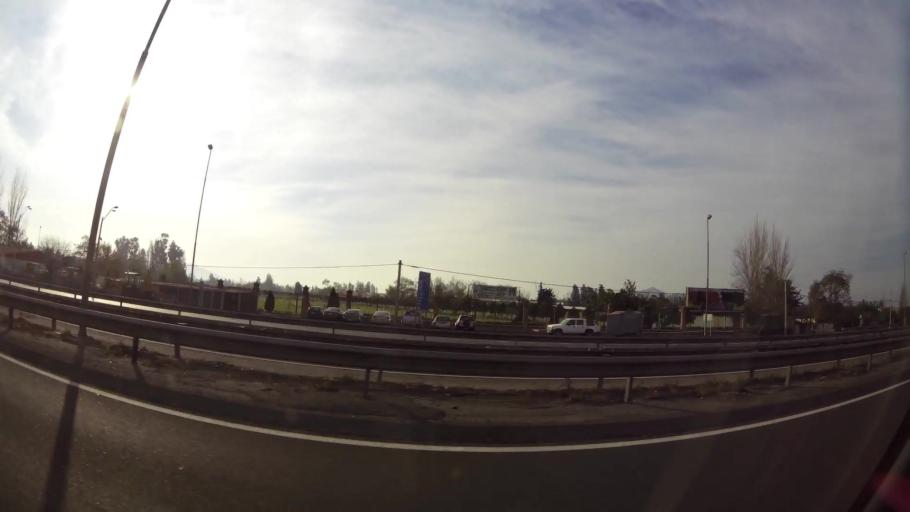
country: CL
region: Santiago Metropolitan
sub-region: Provincia de Talagante
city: Penaflor
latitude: -33.6081
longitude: -70.8511
